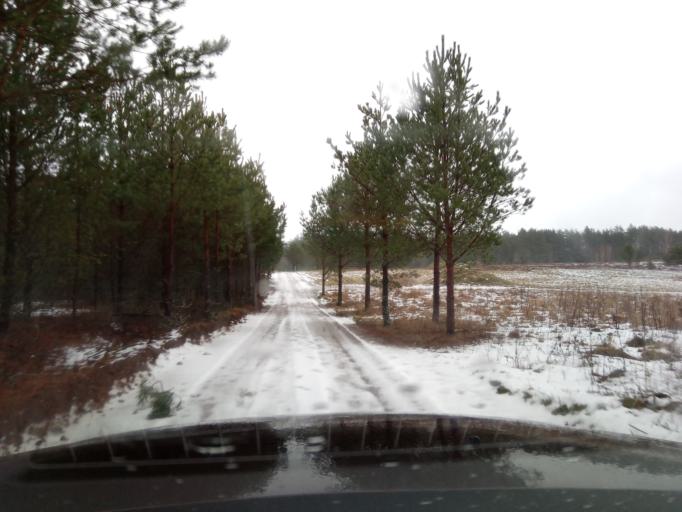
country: LT
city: Svencioneliai
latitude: 55.3352
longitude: 25.8039
